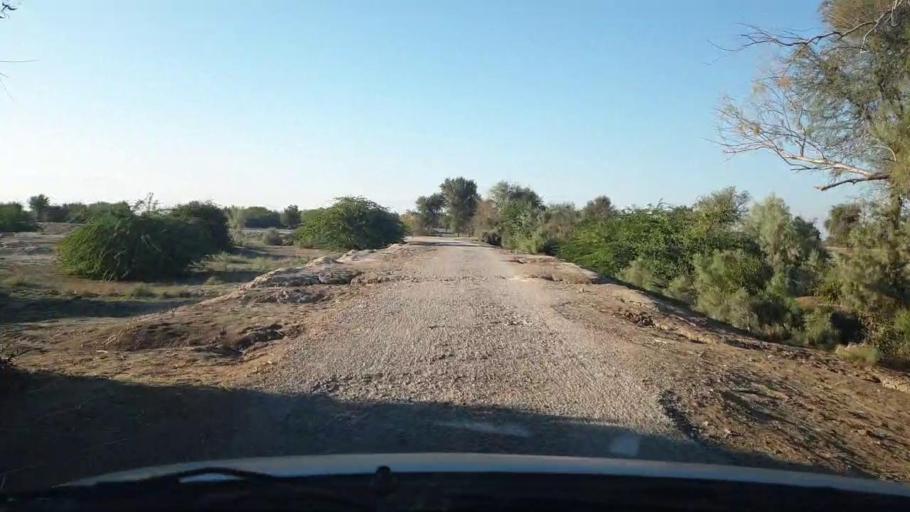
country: PK
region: Sindh
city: Johi
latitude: 26.7749
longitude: 67.4537
